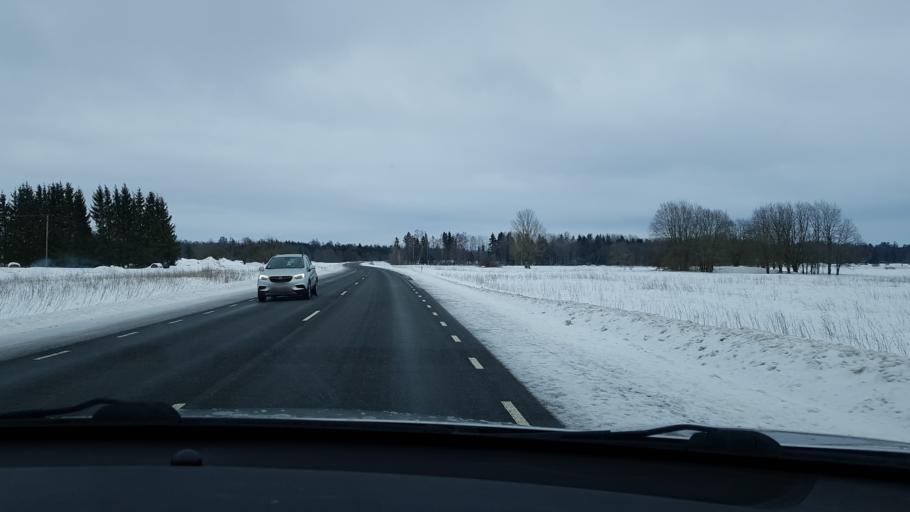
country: EE
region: Jaervamaa
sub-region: Jaerva-Jaani vald
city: Jarva-Jaani
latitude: 59.0822
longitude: 25.8419
